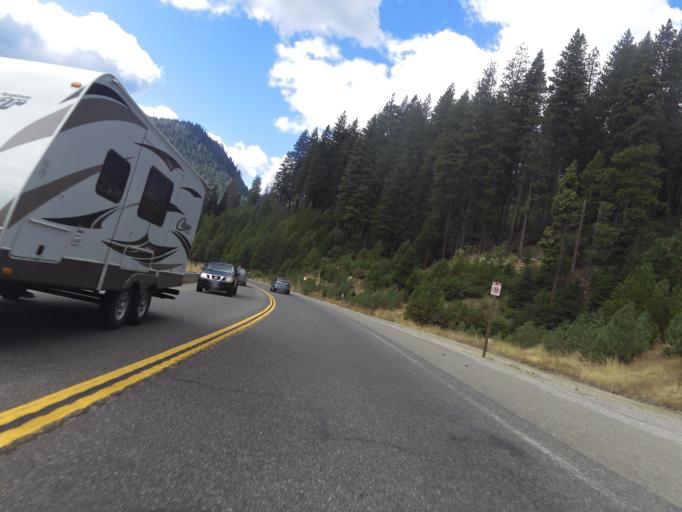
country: US
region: California
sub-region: El Dorado County
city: South Lake Tahoe
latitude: 38.7840
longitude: -120.2371
